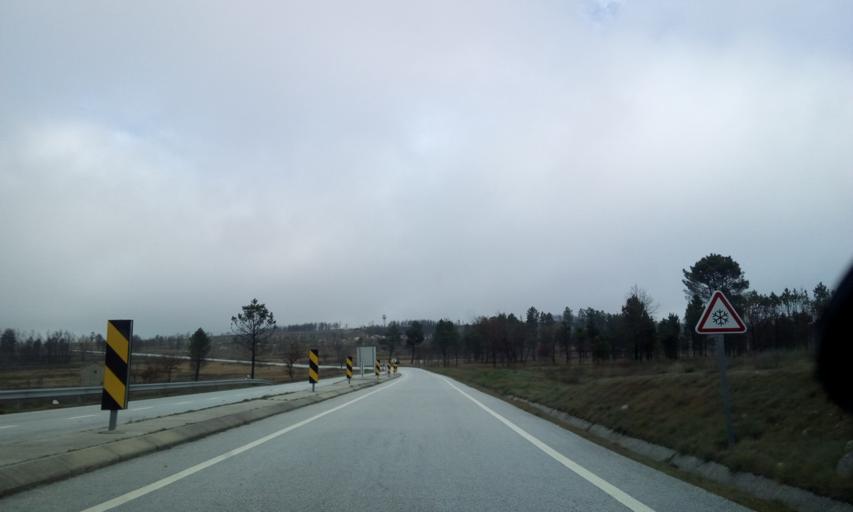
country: PT
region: Guarda
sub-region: Fornos de Algodres
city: Fornos de Algodres
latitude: 40.6958
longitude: -7.4737
